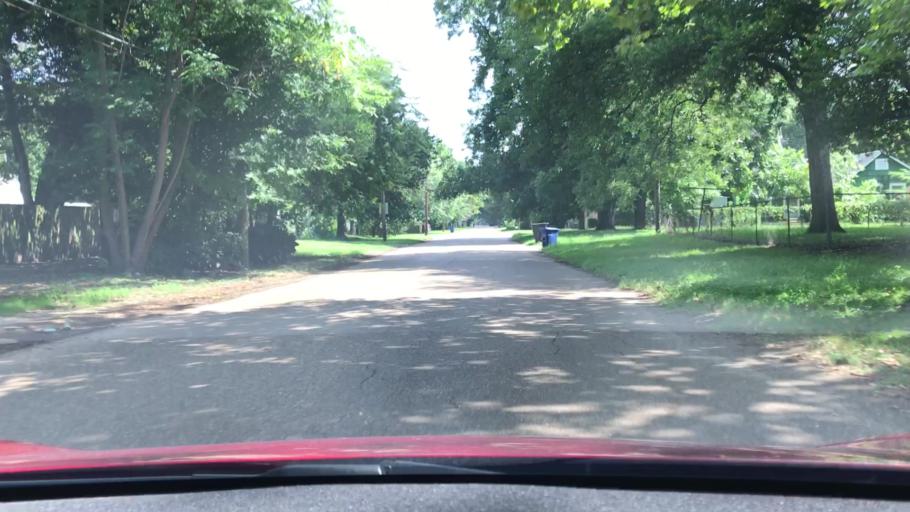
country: US
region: Louisiana
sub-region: Bossier Parish
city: Bossier City
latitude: 32.4762
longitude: -93.7312
